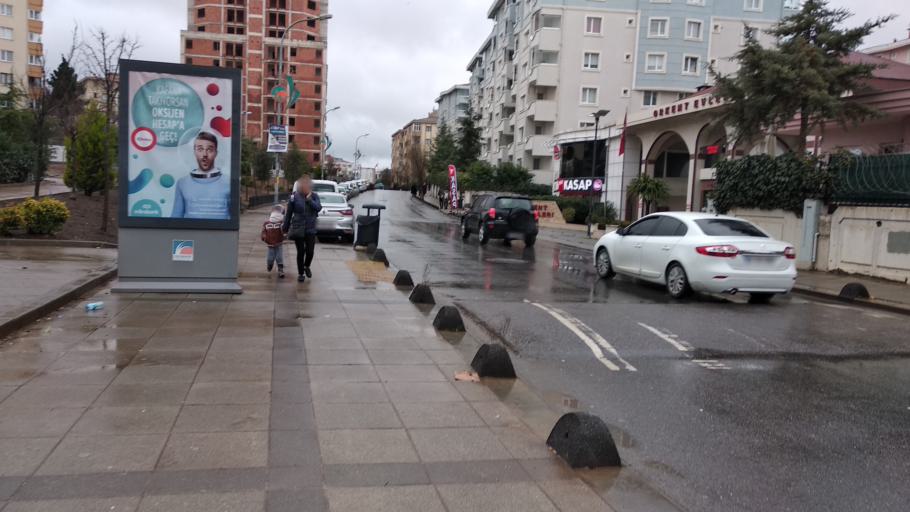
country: TR
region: Istanbul
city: Samandira
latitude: 41.0215
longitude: 29.1880
